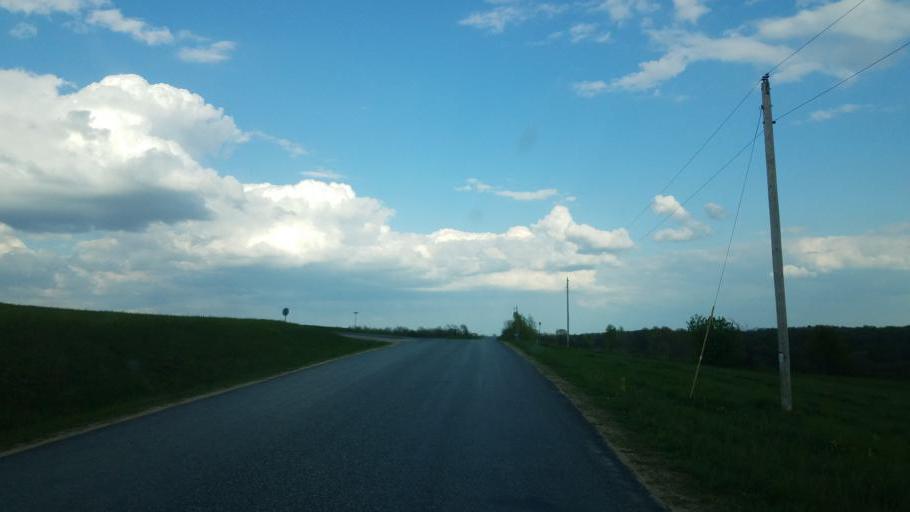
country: US
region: Wisconsin
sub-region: Vernon County
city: Hillsboro
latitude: 43.6852
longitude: -90.3835
